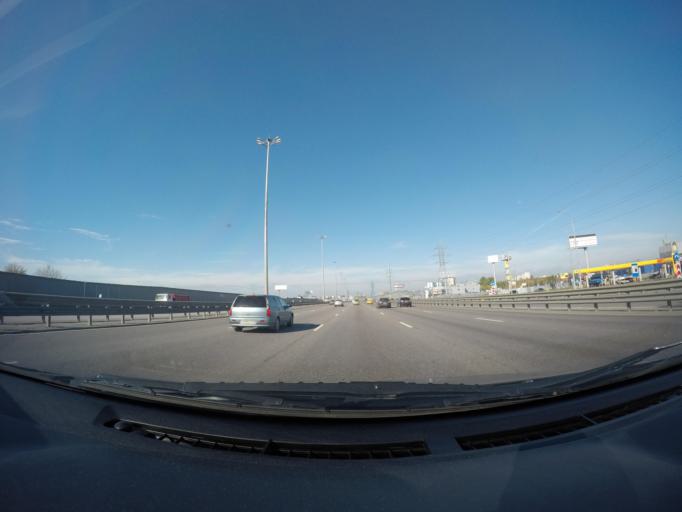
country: RU
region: Moskovskaya
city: Lyubertsy
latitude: 55.6519
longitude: 37.9048
